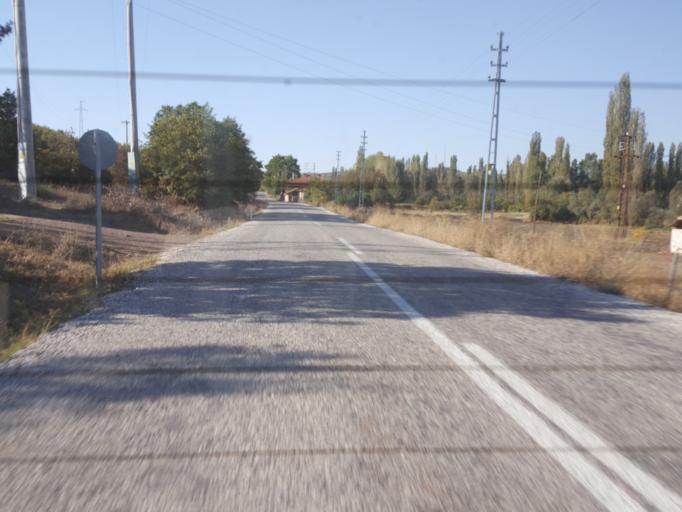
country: TR
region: Corum
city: Seydim
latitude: 40.5507
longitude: 34.7537
